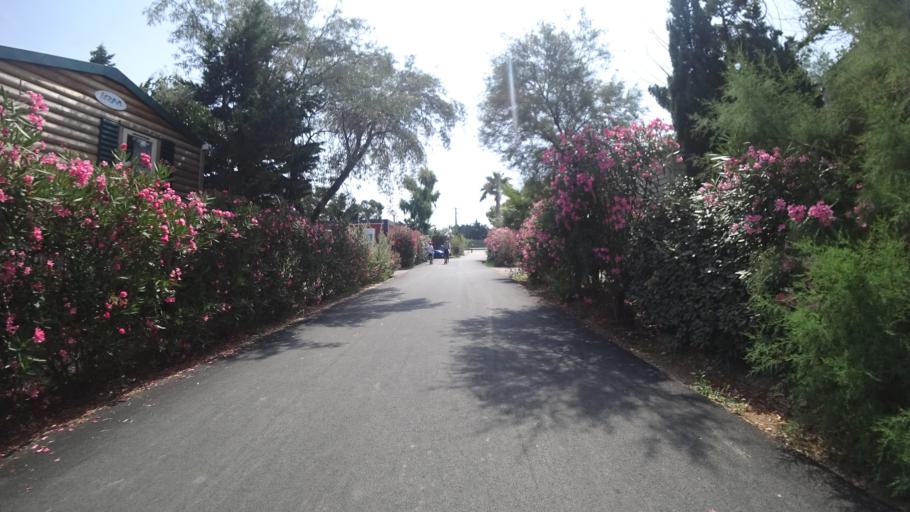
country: FR
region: Languedoc-Roussillon
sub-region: Departement des Pyrenees-Orientales
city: Le Barcares
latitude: 42.7846
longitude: 3.0209
